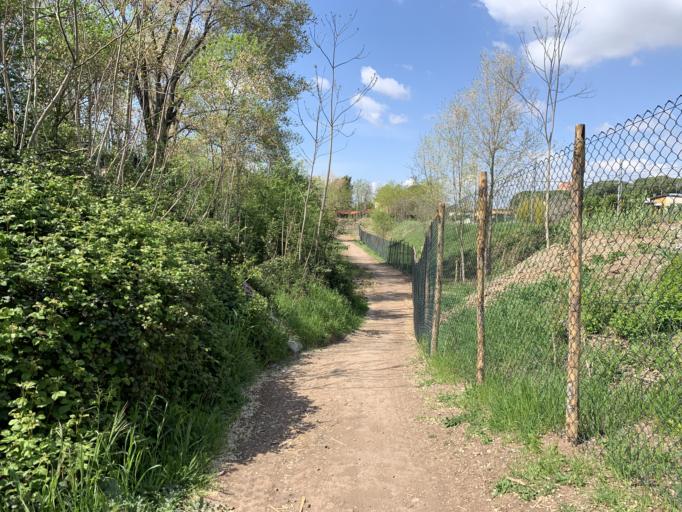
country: IT
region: Latium
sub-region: Citta metropolitana di Roma Capitale
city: Rome
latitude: 41.8545
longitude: 12.5501
